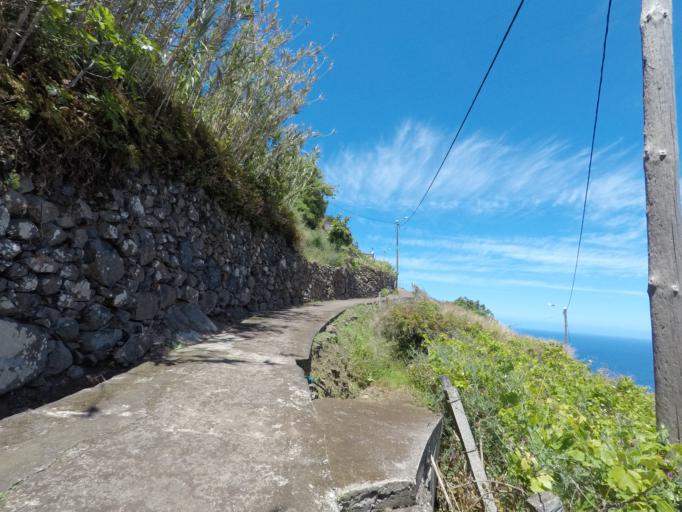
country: PT
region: Madeira
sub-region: Sao Vicente
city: Sao Vicente
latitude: 32.8253
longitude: -16.9789
